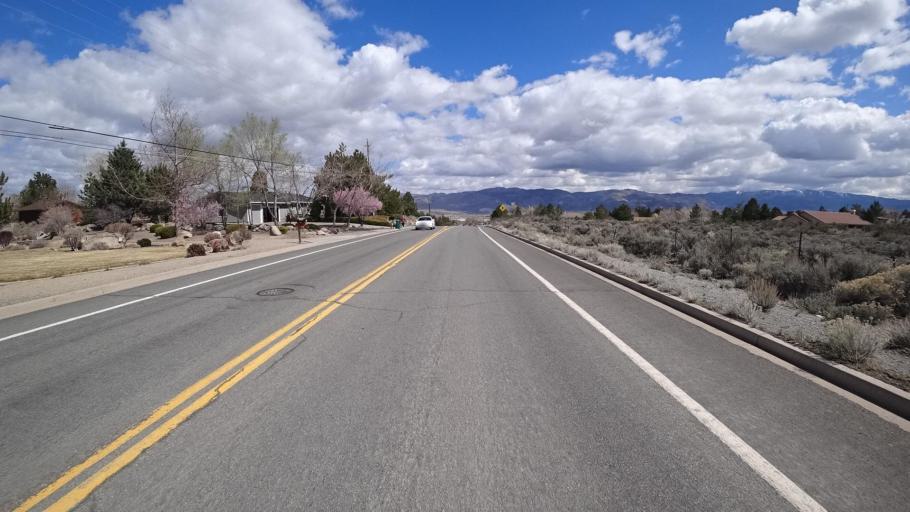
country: US
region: Nevada
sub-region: Washoe County
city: Reno
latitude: 39.4187
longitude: -119.7838
